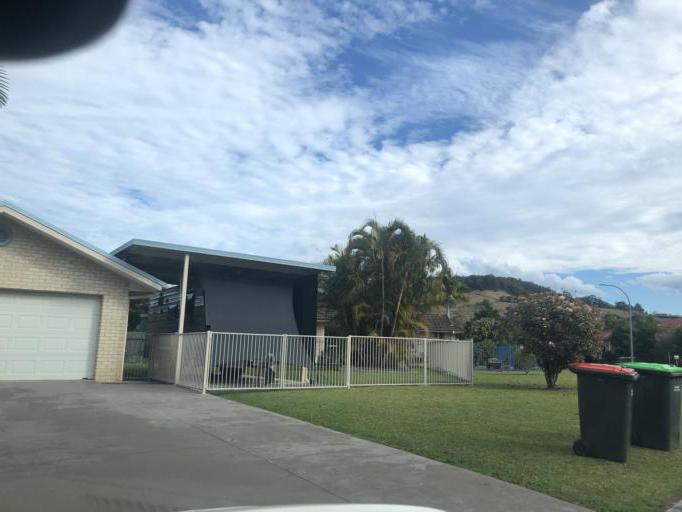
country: AU
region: New South Wales
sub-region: Coffs Harbour
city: Coffs Harbour
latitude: -30.2850
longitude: 153.0990
